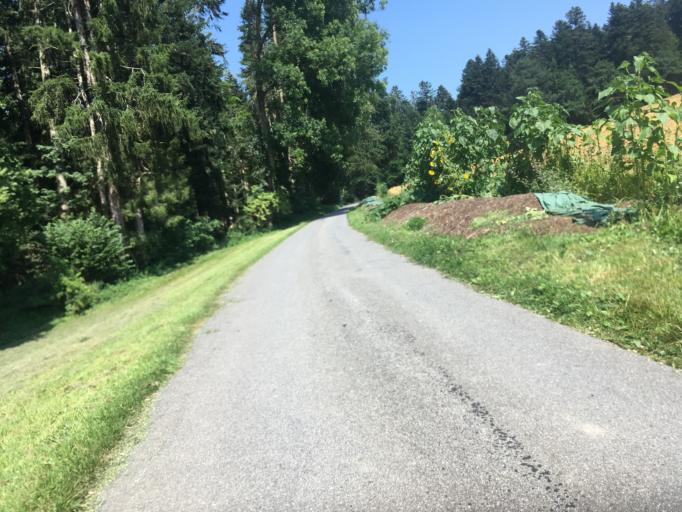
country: CH
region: Bern
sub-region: Emmental District
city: Langnau
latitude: 46.9371
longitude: 7.7578
